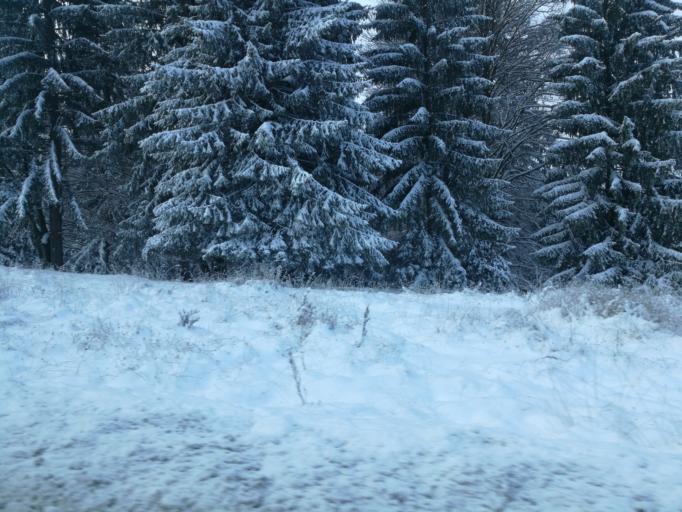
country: RO
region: Brasov
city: Brasov
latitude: 45.6073
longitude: 25.5544
